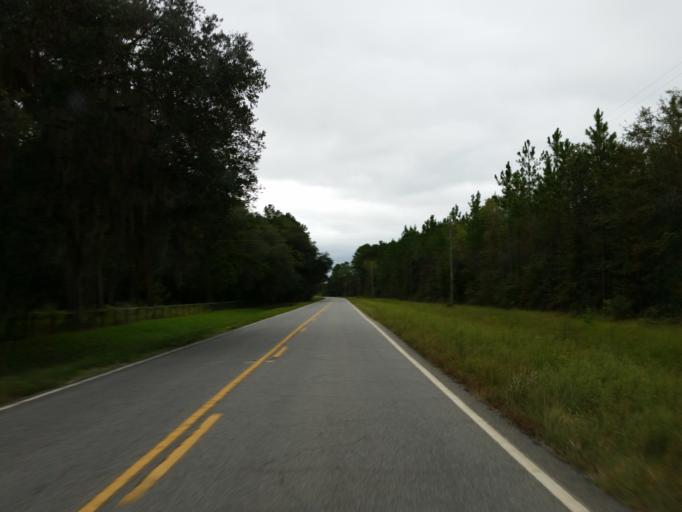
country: US
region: Georgia
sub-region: Echols County
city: Statenville
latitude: 30.8665
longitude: -83.0011
